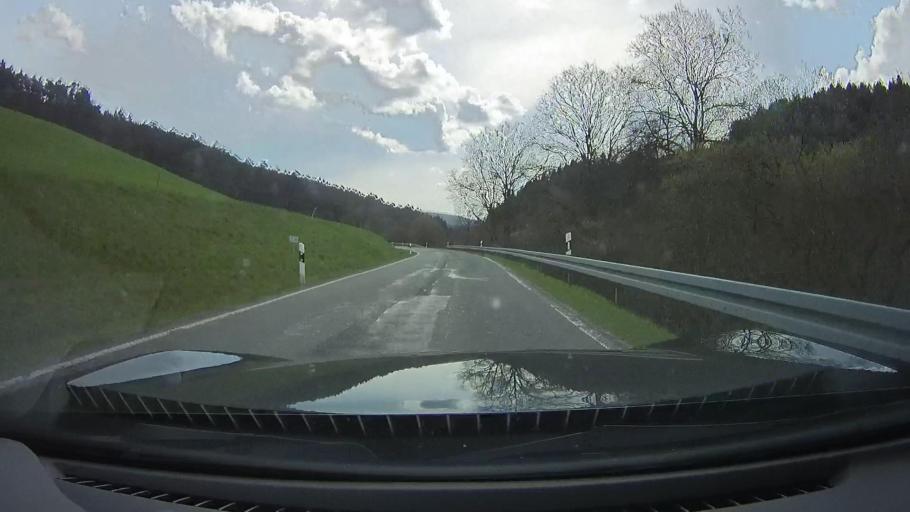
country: DE
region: Bavaria
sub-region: Regierungsbezirk Unterfranken
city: Kirchzell
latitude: 49.5899
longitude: 9.1551
